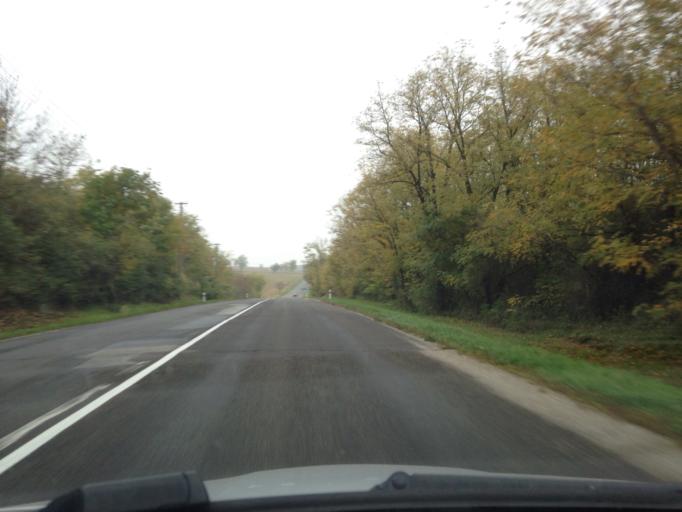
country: SK
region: Nitriansky
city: Svodin
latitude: 47.8720
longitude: 18.4542
